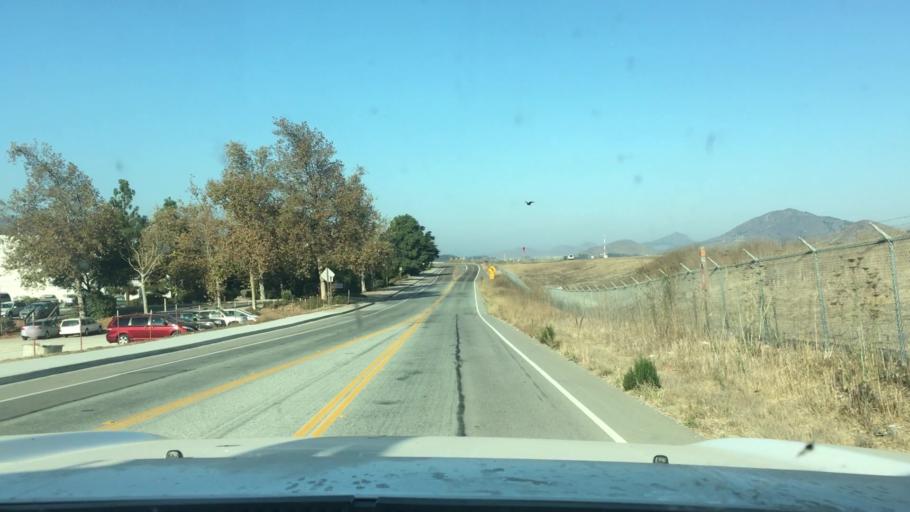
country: US
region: California
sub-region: San Luis Obispo County
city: San Luis Obispo
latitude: 35.2341
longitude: -120.6375
